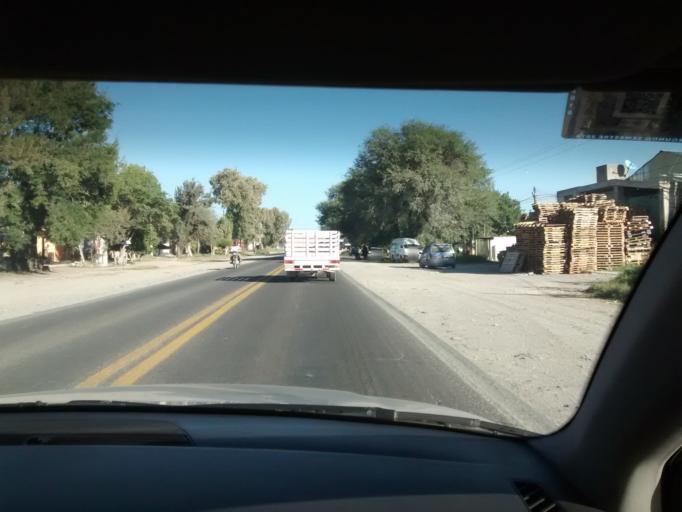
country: MX
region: Puebla
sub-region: Tehuacan
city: Magdalena Cuayucatepec
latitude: 18.5075
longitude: -97.4870
